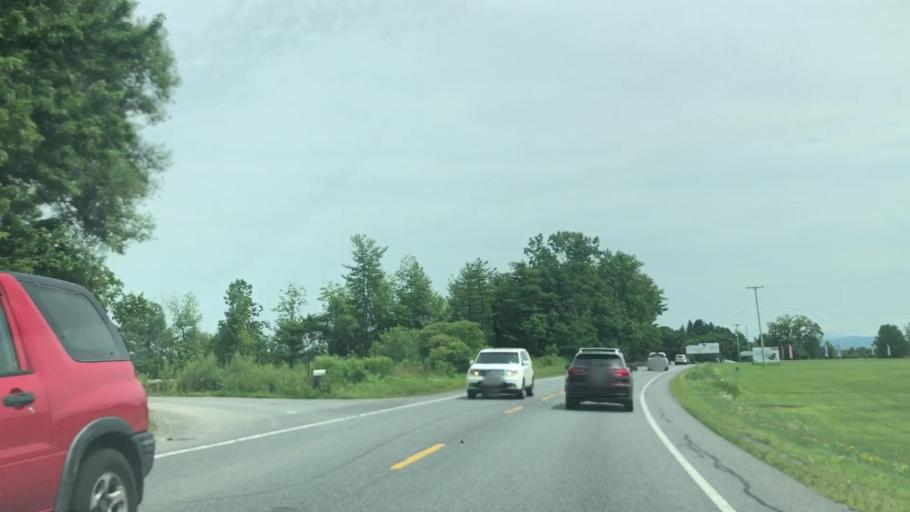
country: US
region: New York
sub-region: Warren County
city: Queensbury
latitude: 43.4060
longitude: -73.5469
